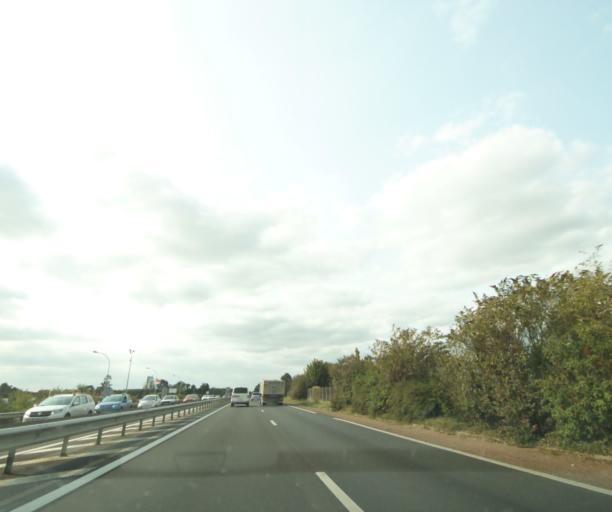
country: FR
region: Centre
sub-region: Departement d'Indre-et-Loire
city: Esvres
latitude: 47.3005
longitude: 0.7973
